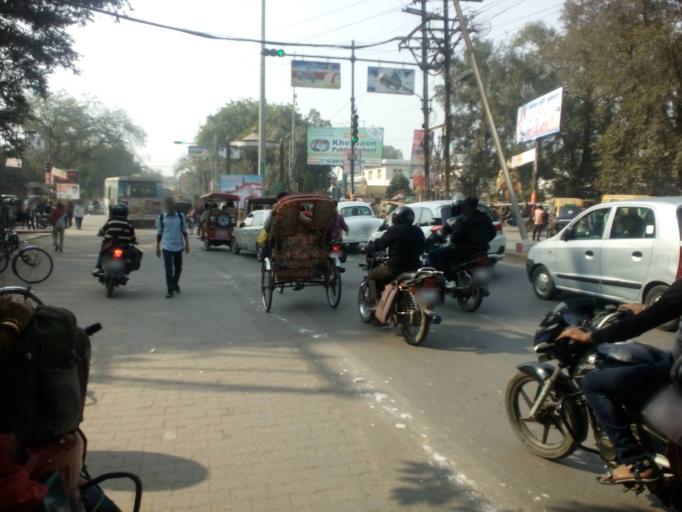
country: IN
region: Uttar Pradesh
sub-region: Allahabad
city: Allahabad
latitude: 25.4495
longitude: 81.8421
